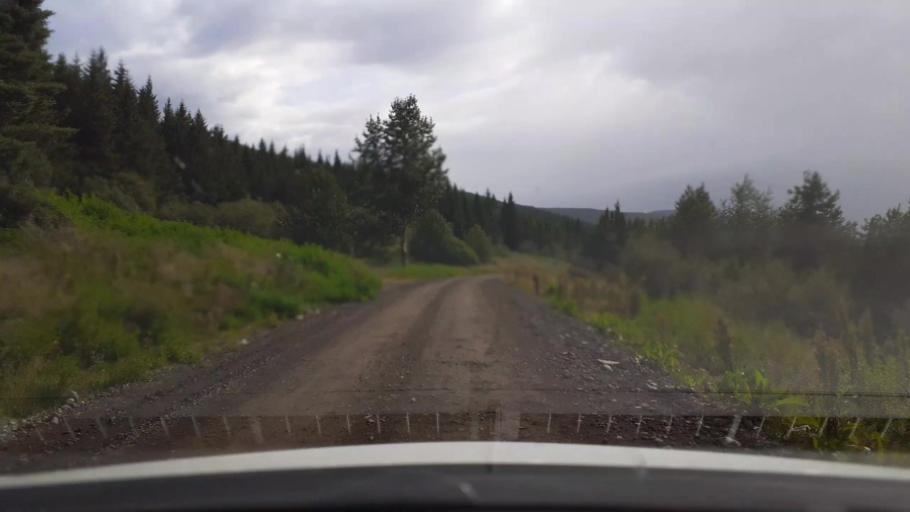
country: IS
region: Capital Region
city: Mosfellsbaer
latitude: 64.5205
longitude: -21.4395
